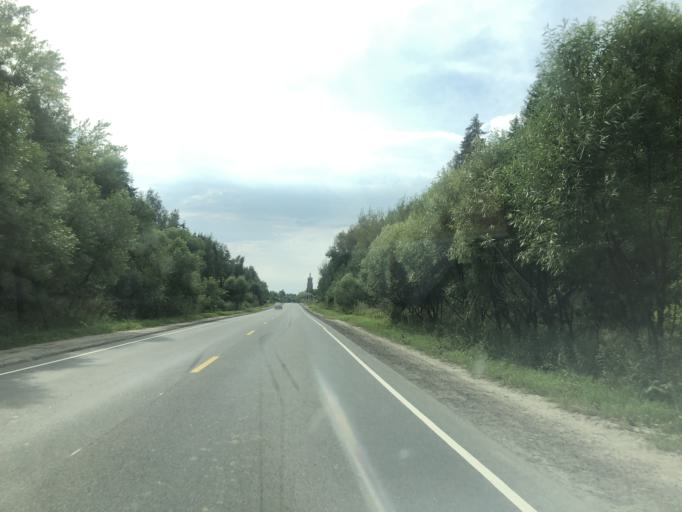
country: RU
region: Ivanovo
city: Shuya
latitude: 56.8534
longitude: 41.5618
